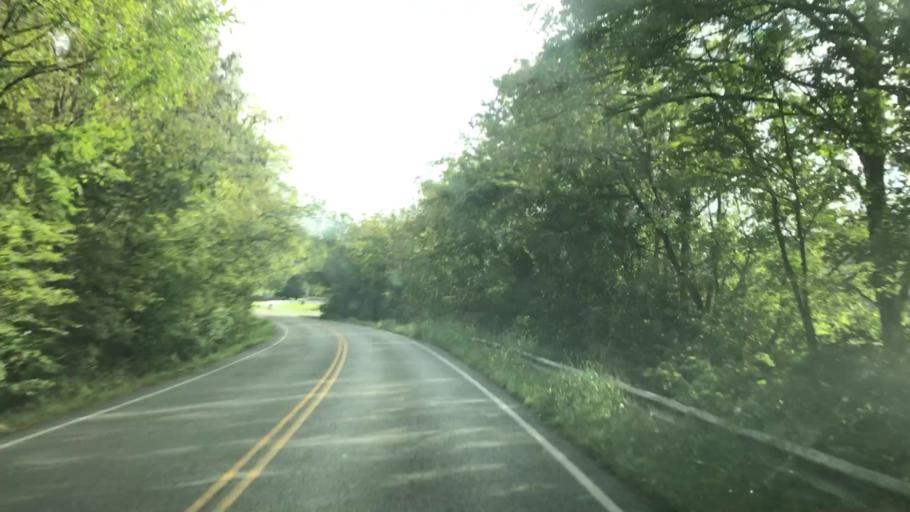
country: US
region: Tennessee
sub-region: Davidson County
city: Forest Hills
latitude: 36.0483
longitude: -86.9040
